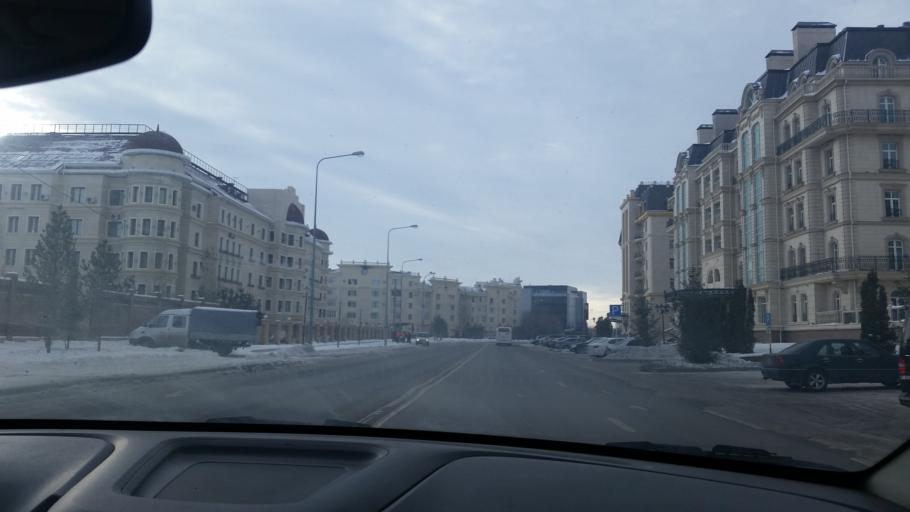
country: KZ
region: Astana Qalasy
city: Astana
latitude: 51.1423
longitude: 71.4512
